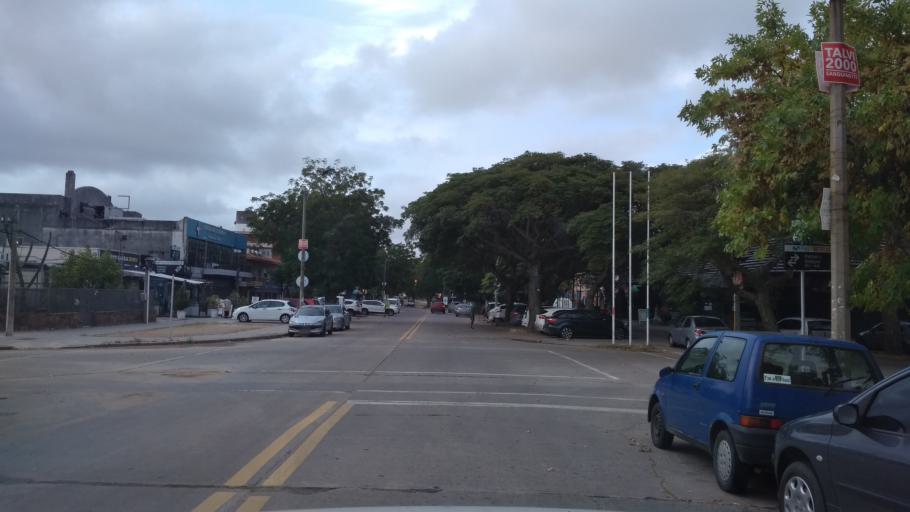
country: UY
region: Canelones
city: Paso de Carrasco
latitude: -34.8939
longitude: -56.0801
